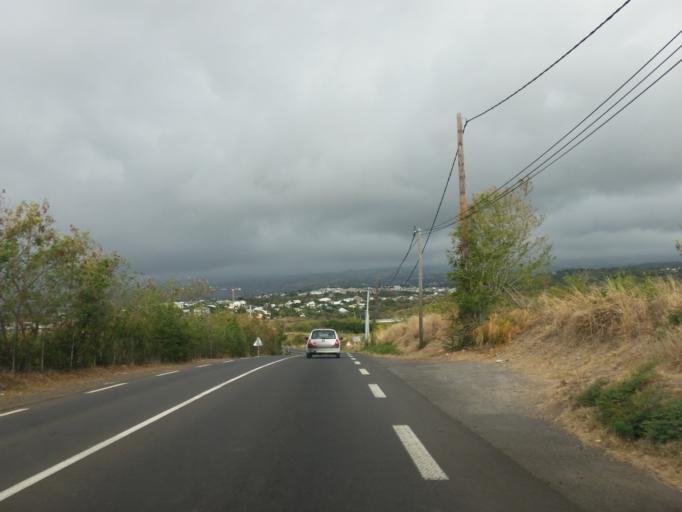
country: RE
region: Reunion
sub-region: Reunion
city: Saint-Paul
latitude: -21.0430
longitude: 55.2437
